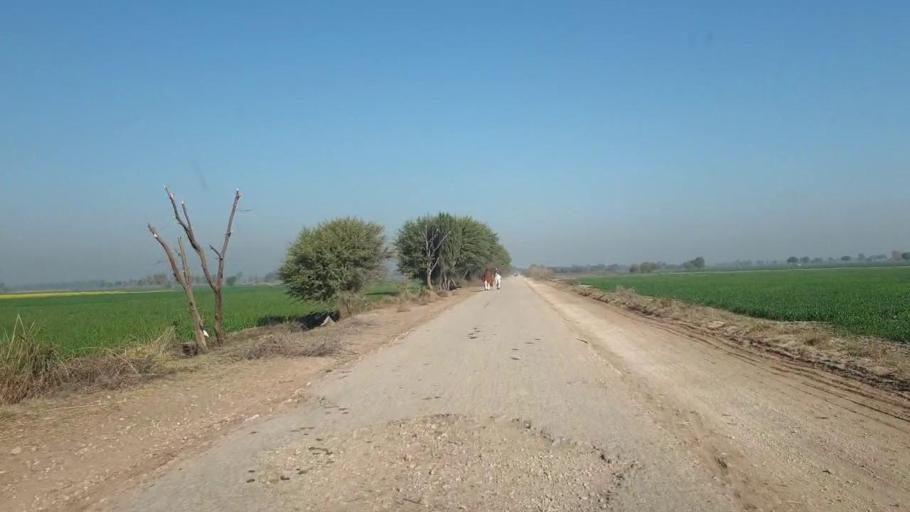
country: PK
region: Sindh
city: Shahdadpur
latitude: 25.9256
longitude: 68.5063
